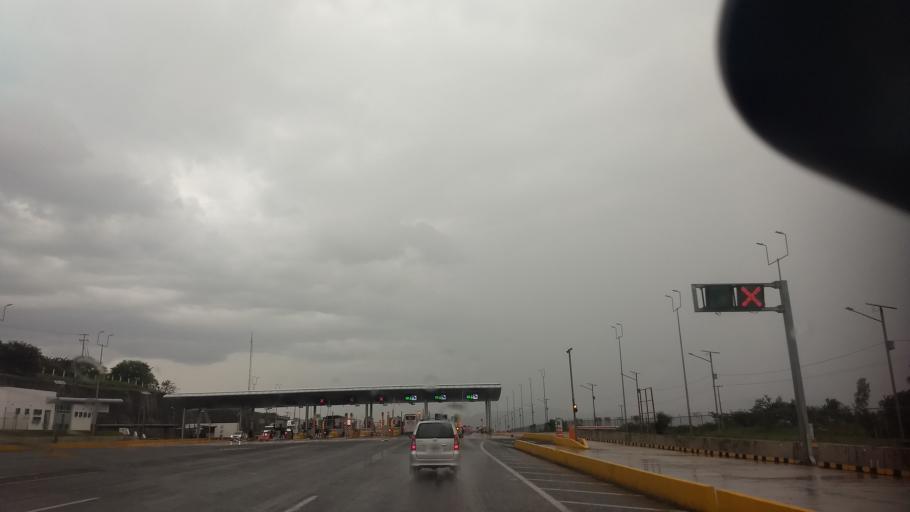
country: MX
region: Jalisco
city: Tonila
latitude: 19.4083
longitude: -103.5287
